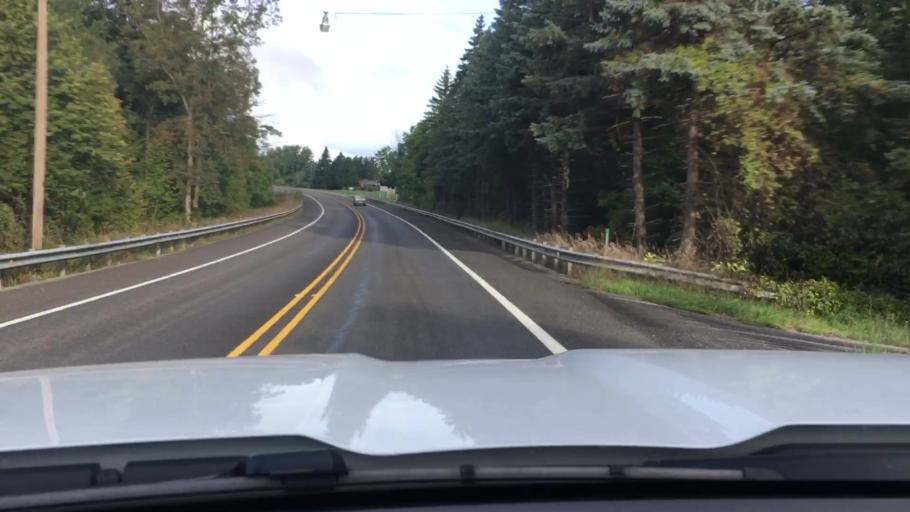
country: US
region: Michigan
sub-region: Tuscola County
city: Caro
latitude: 43.3422
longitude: -83.3569
